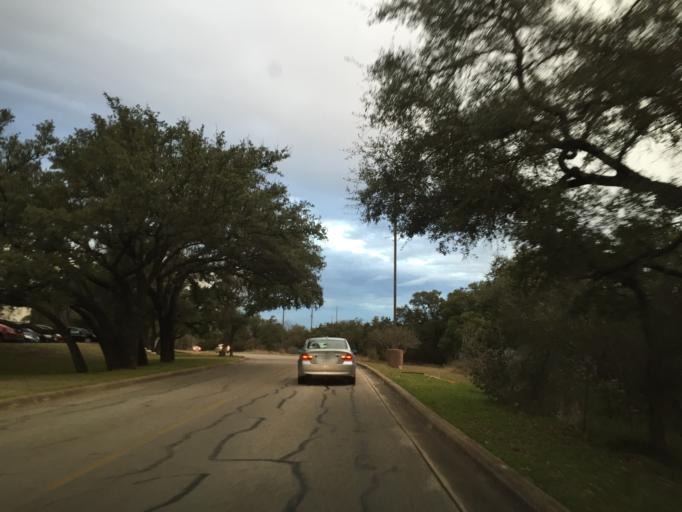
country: US
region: Texas
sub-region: Williamson County
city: Jollyville
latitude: 30.4341
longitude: -97.7500
